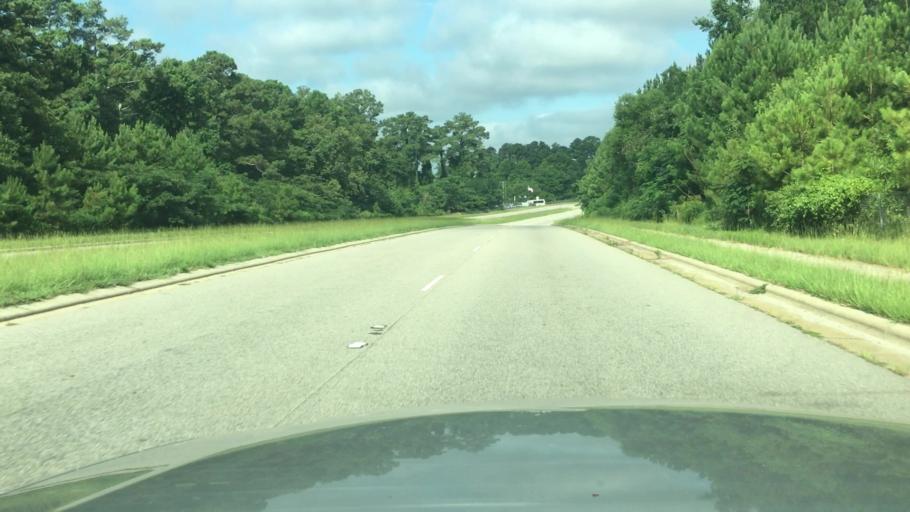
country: US
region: North Carolina
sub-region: Cumberland County
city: Hope Mills
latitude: 34.9915
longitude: -78.9562
